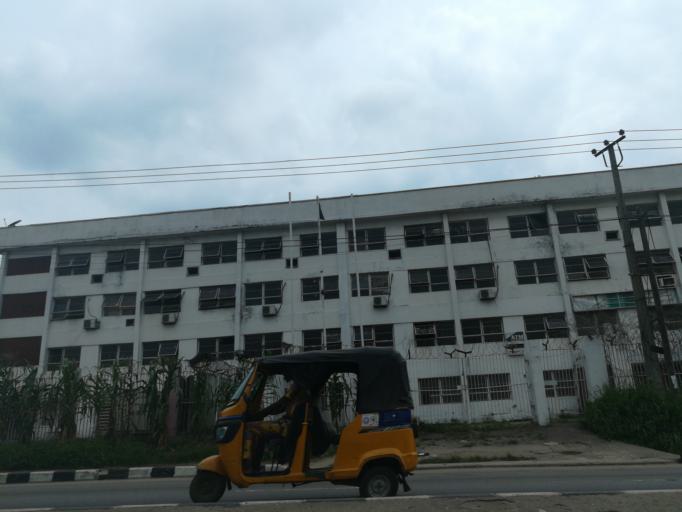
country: NG
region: Lagos
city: Ikeja
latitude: 6.6082
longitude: 3.3574
